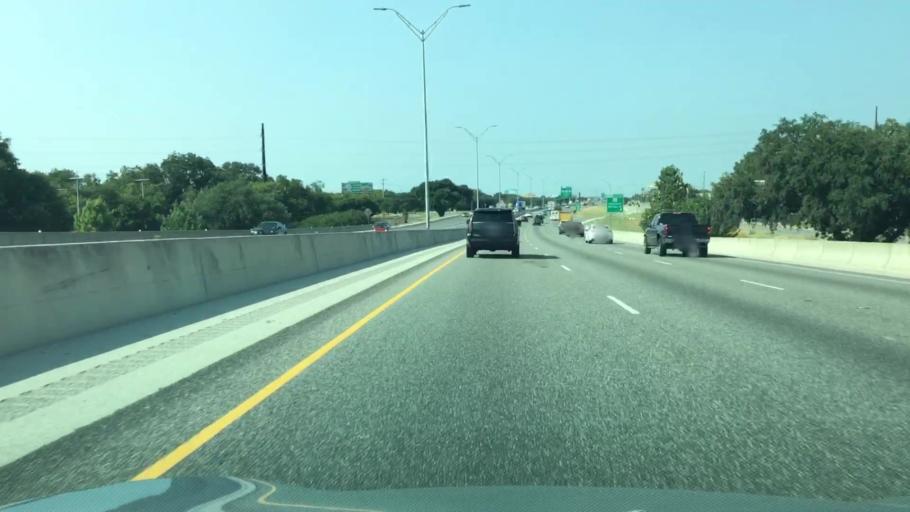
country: US
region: Texas
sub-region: Hays County
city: San Marcos
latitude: 29.9041
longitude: -97.9034
